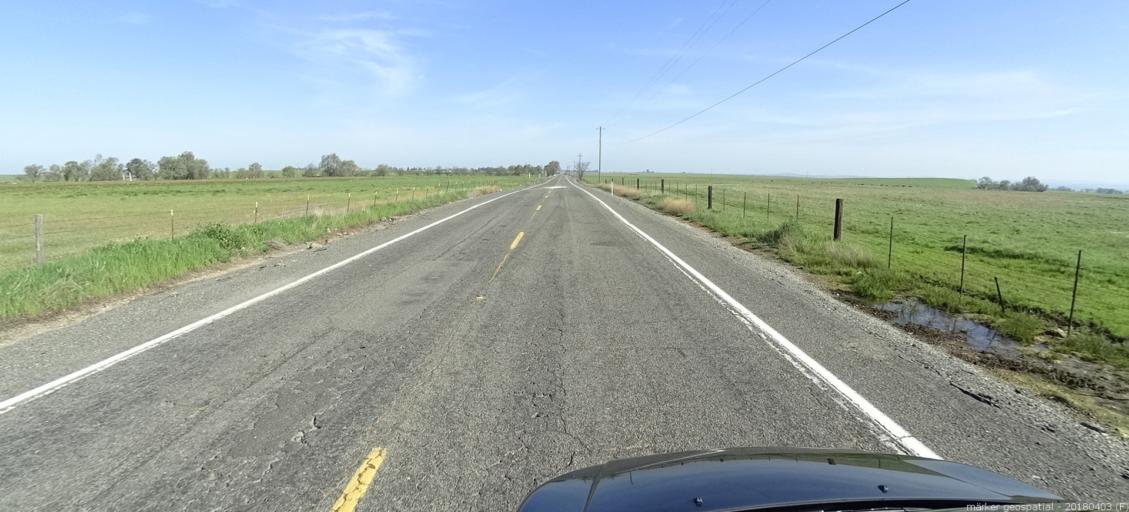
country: US
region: California
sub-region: Sacramento County
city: Clay
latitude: 38.3801
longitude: -121.1685
